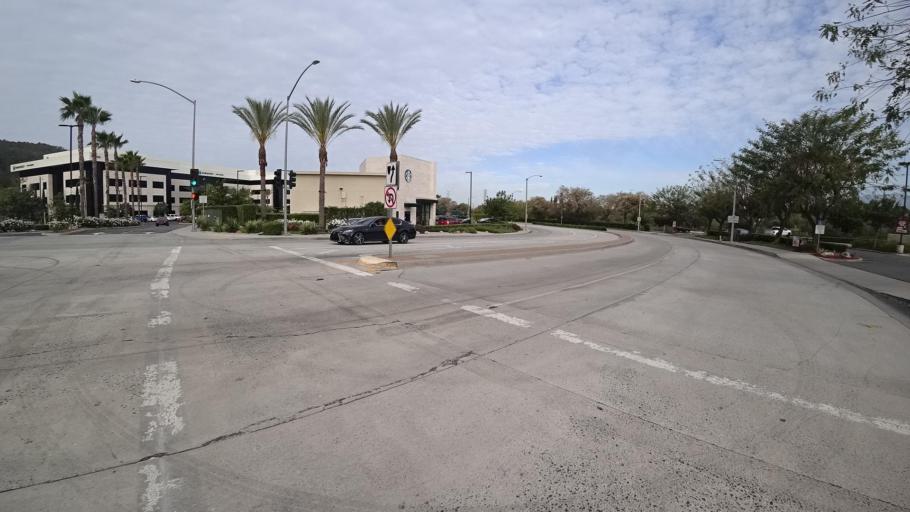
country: US
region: California
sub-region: Los Angeles County
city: Avocado Heights
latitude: 34.0309
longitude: -118.0083
